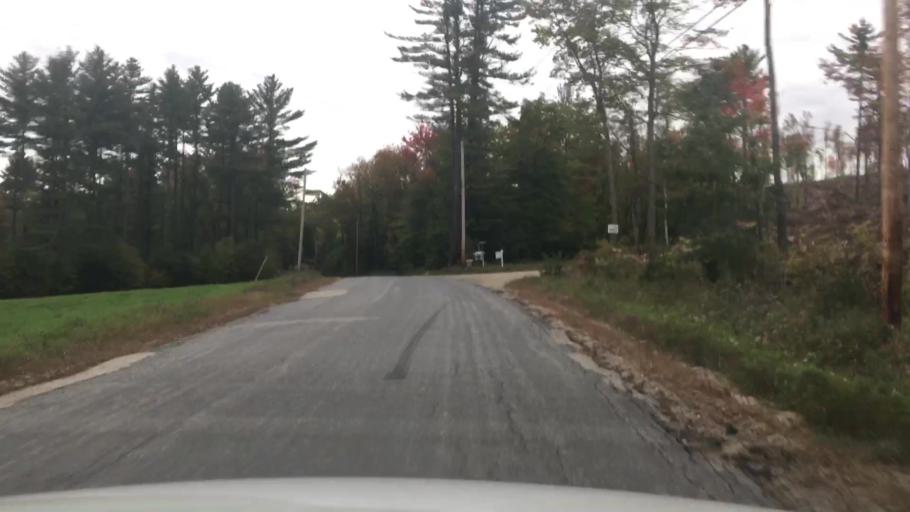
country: US
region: Maine
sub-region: Oxford County
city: Bethel
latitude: 44.4704
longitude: -70.7838
